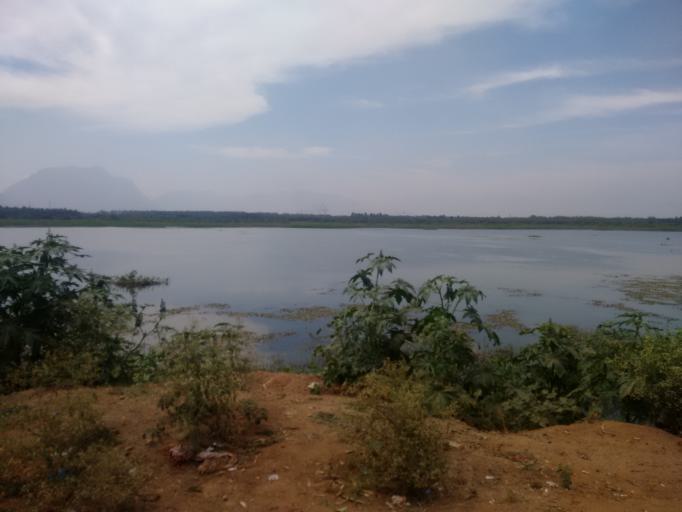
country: IN
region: Tamil Nadu
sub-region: Coimbatore
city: Perur
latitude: 10.9694
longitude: 76.9309
